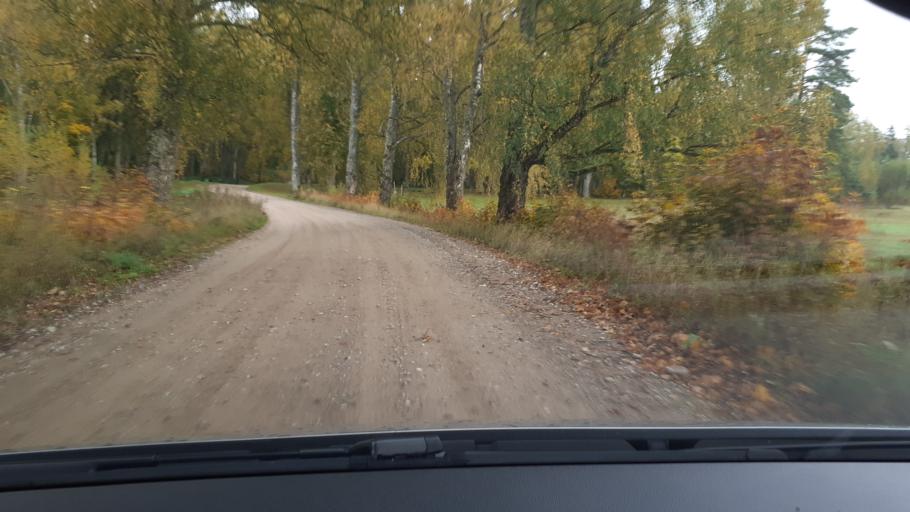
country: LV
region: Kuldigas Rajons
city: Kuldiga
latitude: 57.0290
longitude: 21.9154
